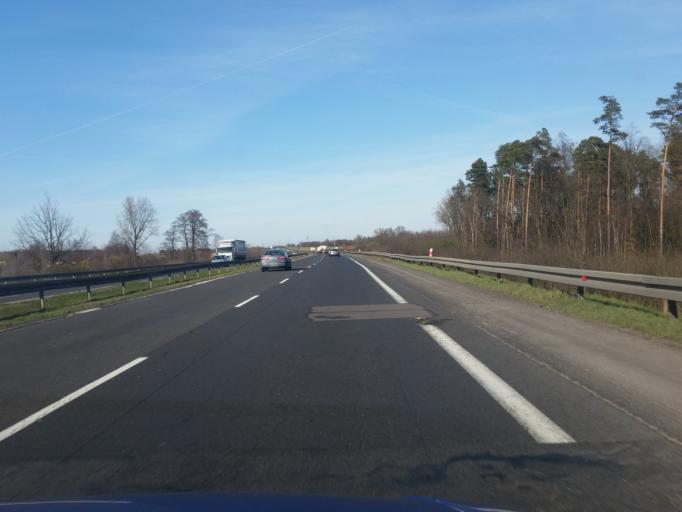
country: PL
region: Lodz Voivodeship
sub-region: Powiat radomszczanski
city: Gomunice
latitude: 51.1713
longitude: 19.4631
